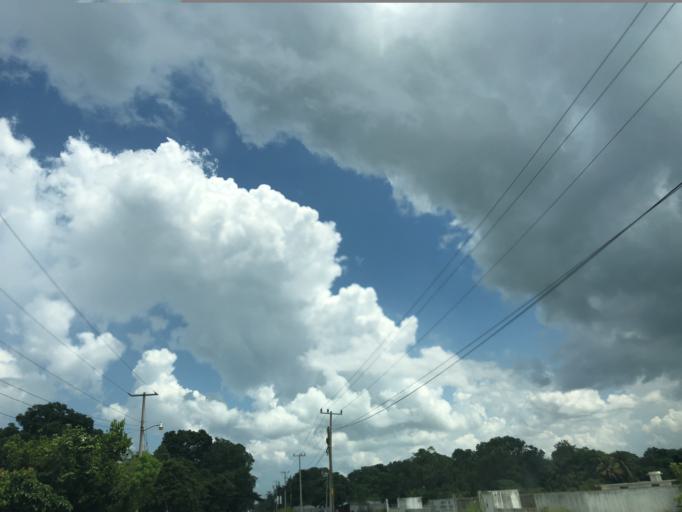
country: MX
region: Tabasco
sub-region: Comalcalco
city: Oriente 6ta. Seccion (Los Mulatos)
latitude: 18.1756
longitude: -93.2360
